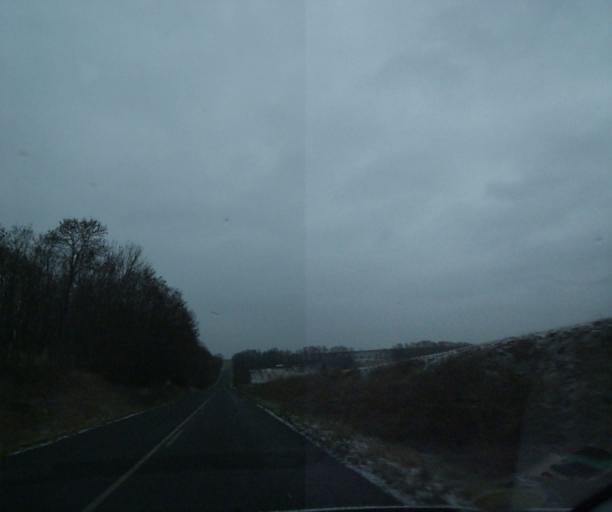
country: FR
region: Champagne-Ardenne
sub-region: Departement de la Haute-Marne
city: Wassy
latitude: 48.4283
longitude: 4.9697
